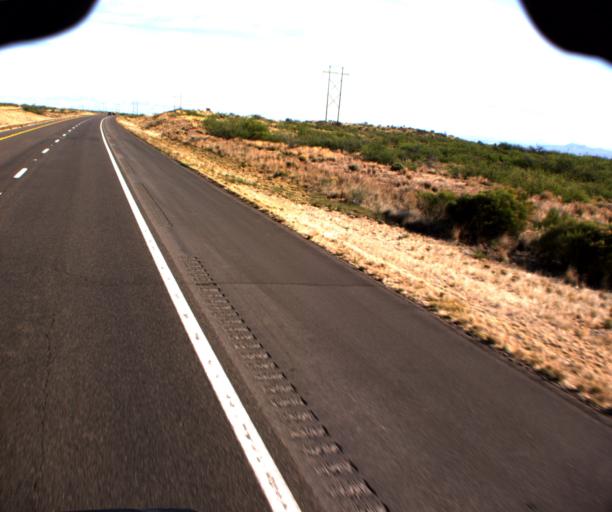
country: US
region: Arizona
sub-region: Graham County
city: Swift Trail Junction
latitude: 32.5153
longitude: -109.6738
